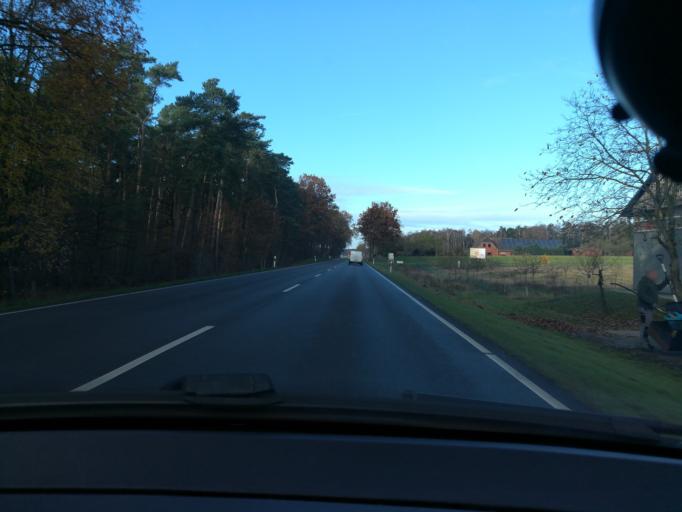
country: DE
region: Lower Saxony
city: Kirchdorf
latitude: 52.5469
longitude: 8.8635
